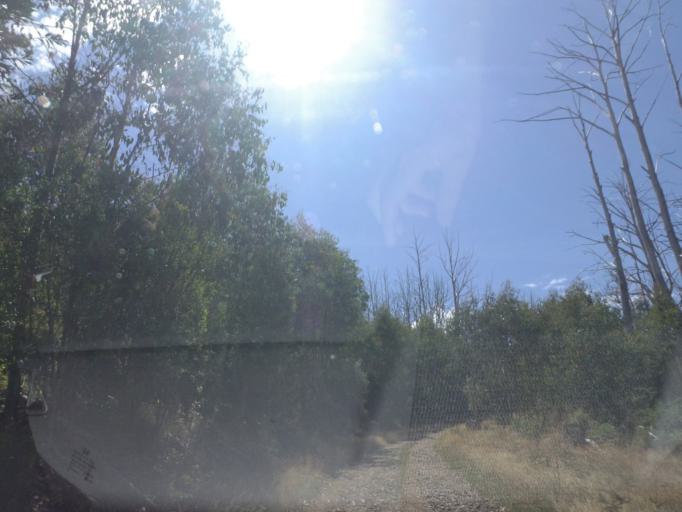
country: AU
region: Victoria
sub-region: Murrindindi
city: Alexandra
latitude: -37.4636
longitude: 145.8345
